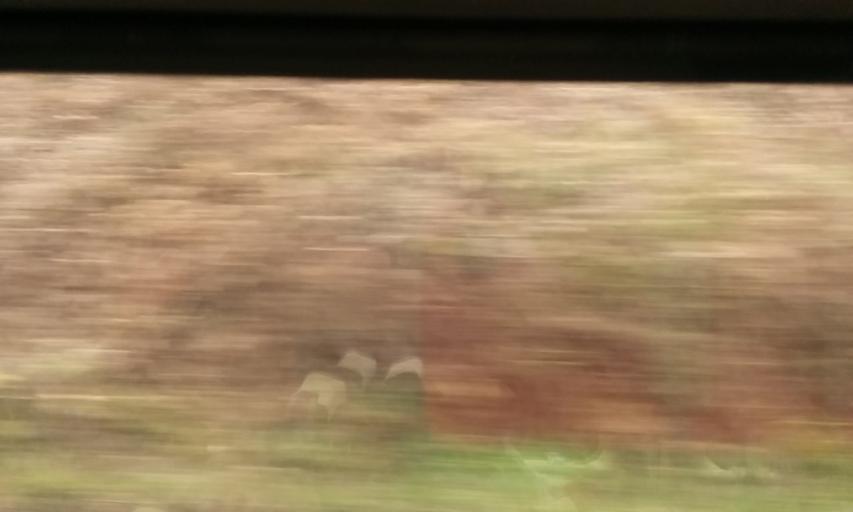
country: JP
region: Gifu
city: Nakatsugawa
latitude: 35.5589
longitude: 137.5338
